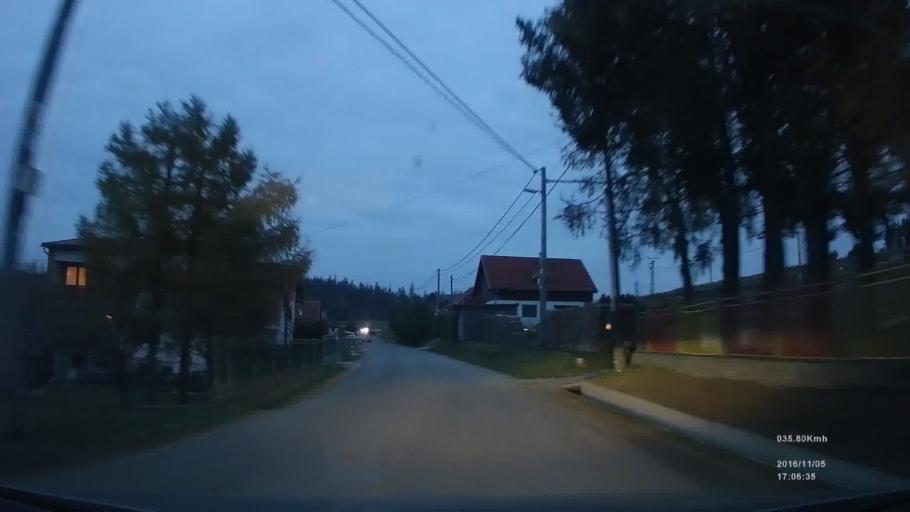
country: SK
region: Presovsky
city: Lubica
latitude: 49.0490
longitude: 20.5019
